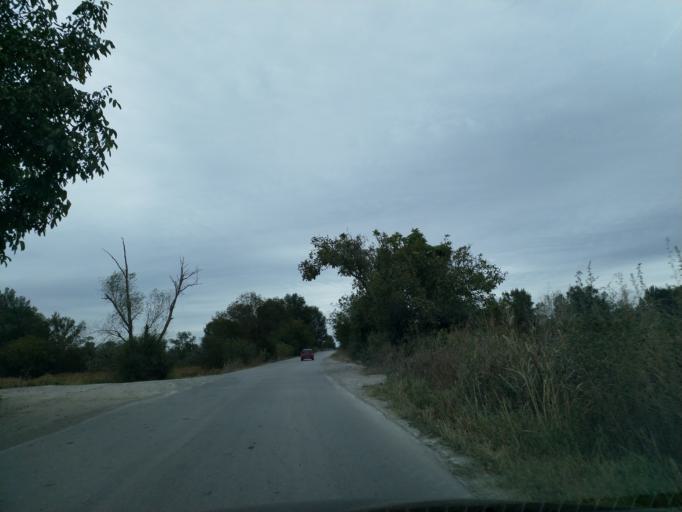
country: RS
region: Central Serbia
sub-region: Pomoravski Okrug
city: Paracin
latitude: 43.8293
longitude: 21.3411
